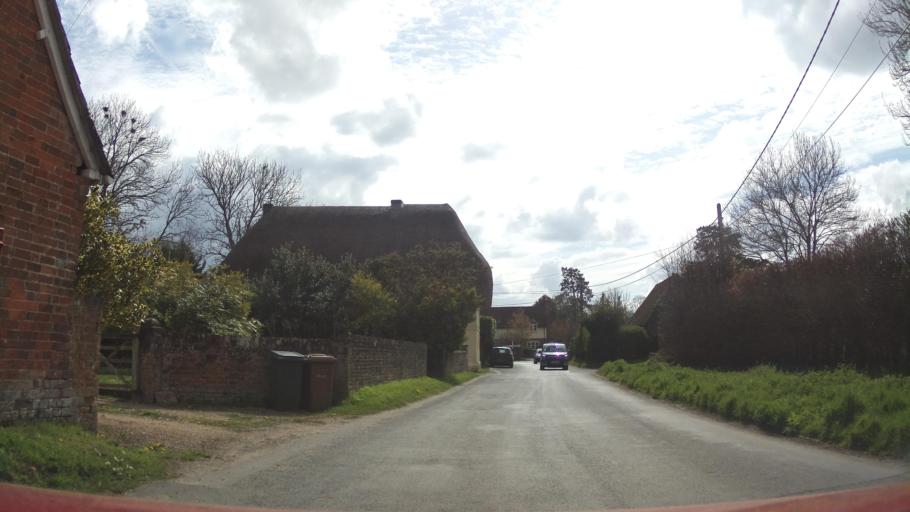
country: GB
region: England
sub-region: Hampshire
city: Romsey
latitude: 51.0831
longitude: -1.5167
